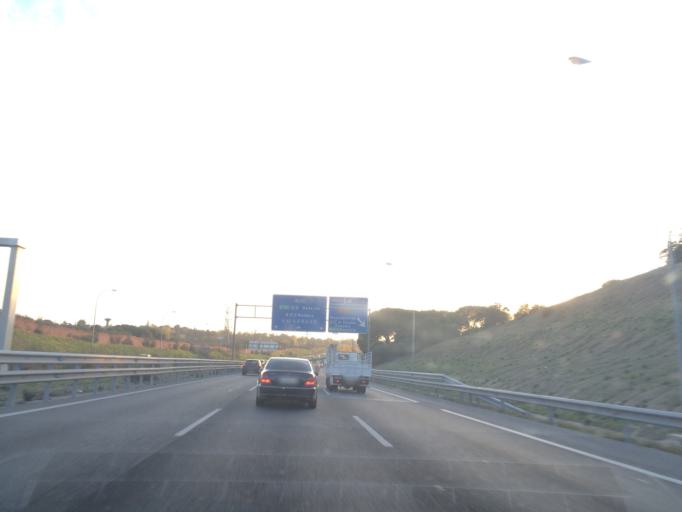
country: ES
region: Madrid
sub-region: Provincia de Madrid
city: Pozuelo de Alarcon
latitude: 40.4507
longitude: -3.8199
